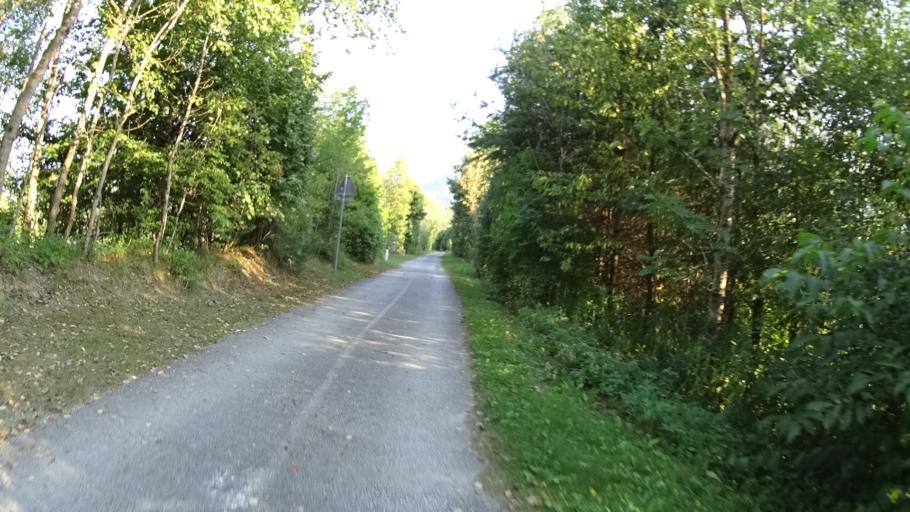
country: AT
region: Carinthia
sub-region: Politischer Bezirk Villach Land
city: Sankt Jakob
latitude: 46.5430
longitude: 14.0890
